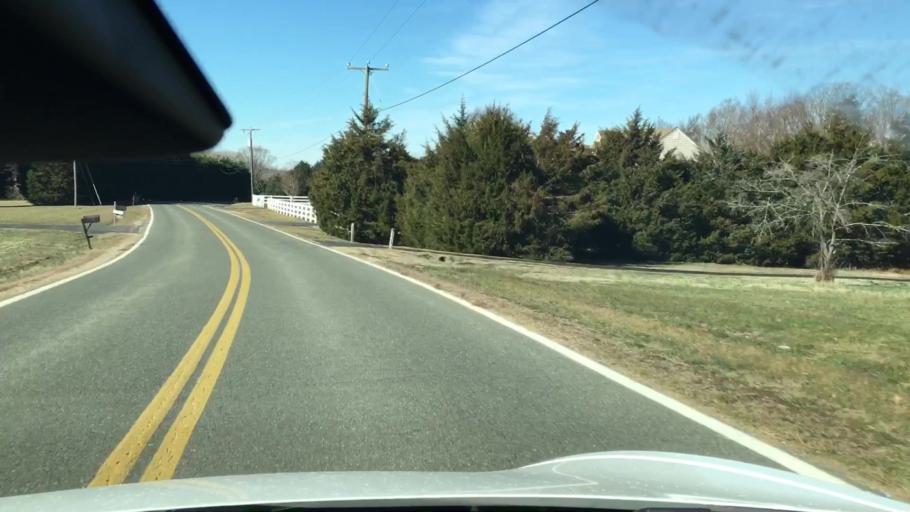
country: US
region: Virginia
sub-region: Powhatan County
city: Powhatan
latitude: 37.5509
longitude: -77.7940
